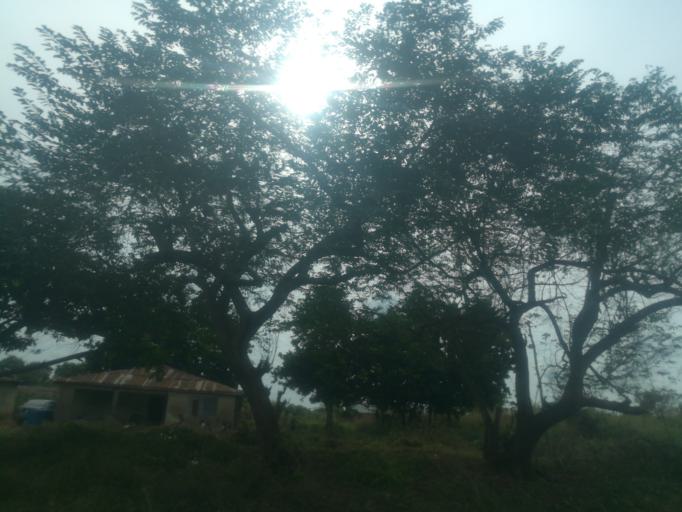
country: NG
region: Ogun
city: Ayetoro
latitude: 7.3295
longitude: 3.0668
